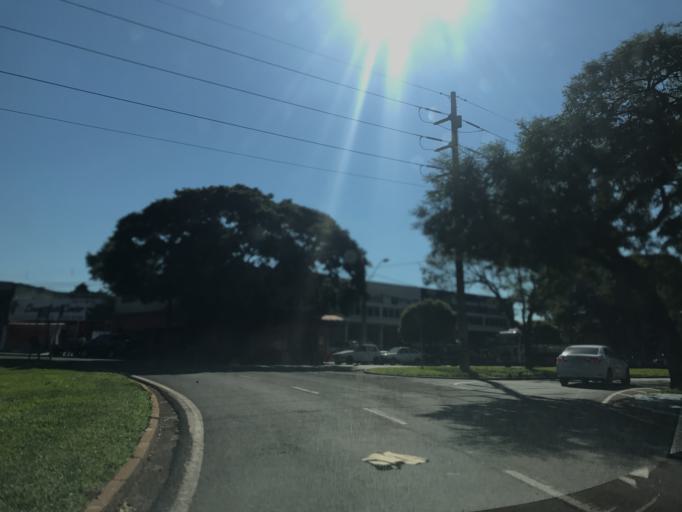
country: BR
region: Parana
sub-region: Maringa
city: Maringa
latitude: -23.4496
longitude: -51.9539
